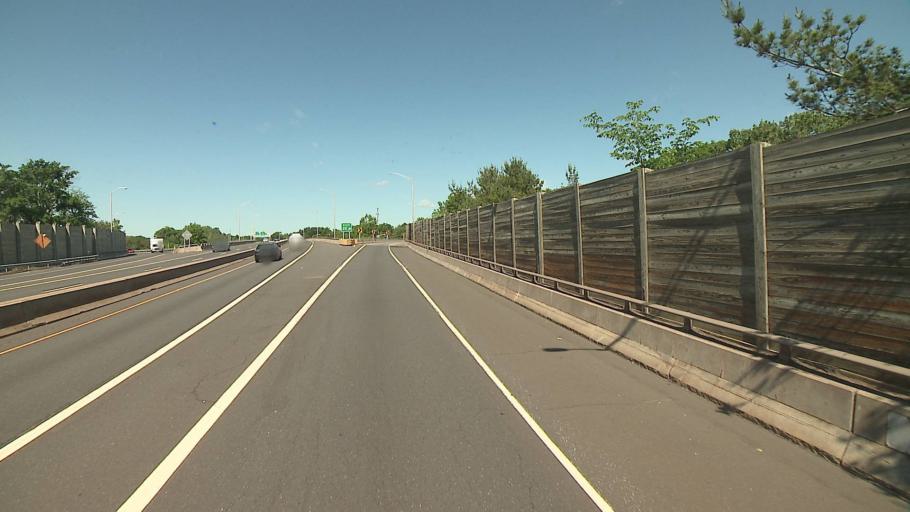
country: US
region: Connecticut
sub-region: Hartford County
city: Blue Hills
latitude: 41.8191
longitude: -72.6614
